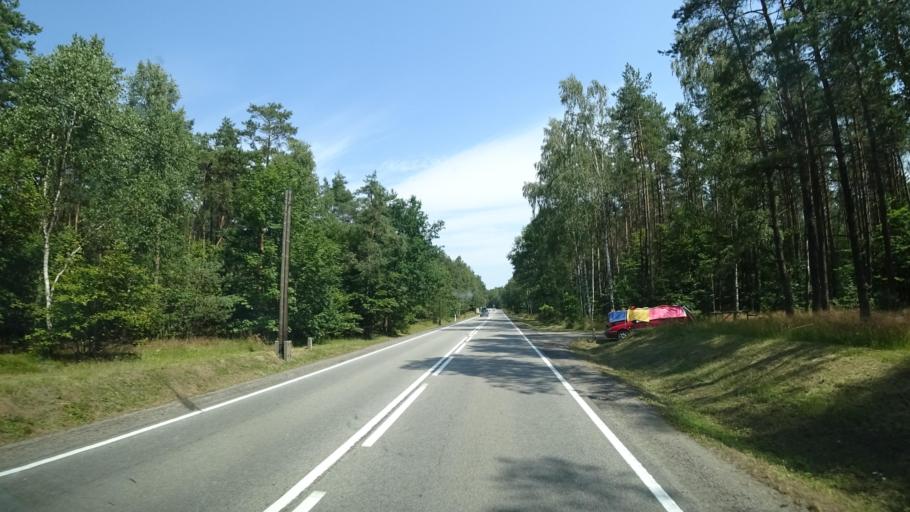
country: PL
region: Pomeranian Voivodeship
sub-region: Powiat koscierski
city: Grabowo Koscierskie
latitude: 54.1756
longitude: 18.0761
